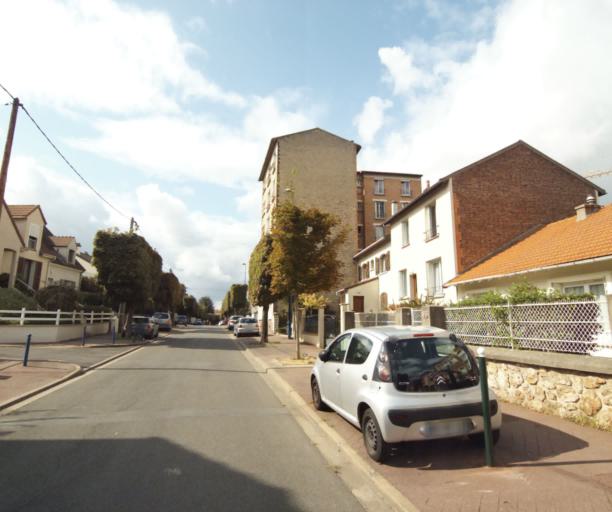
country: FR
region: Ile-de-France
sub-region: Departement des Hauts-de-Seine
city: Clamart
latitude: 48.8104
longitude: 2.2636
